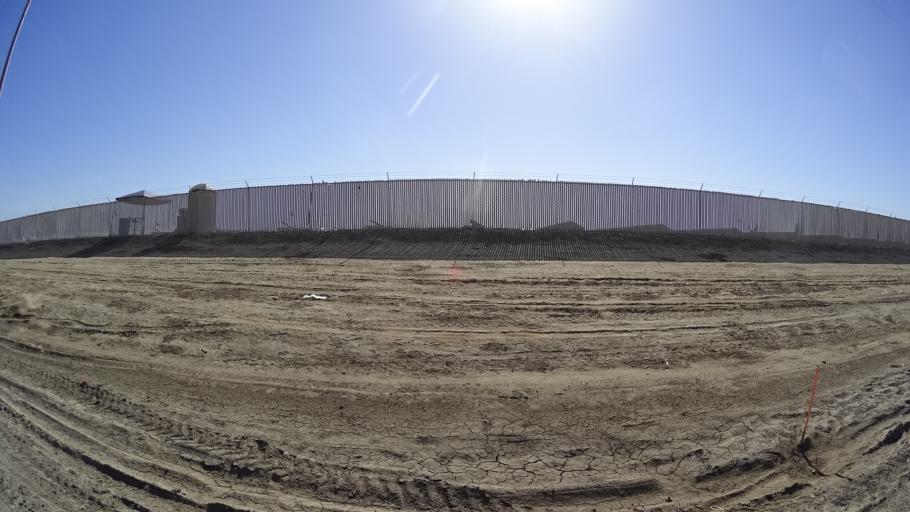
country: US
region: California
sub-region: Kings County
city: Corcoran
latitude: 36.1979
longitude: -119.5646
